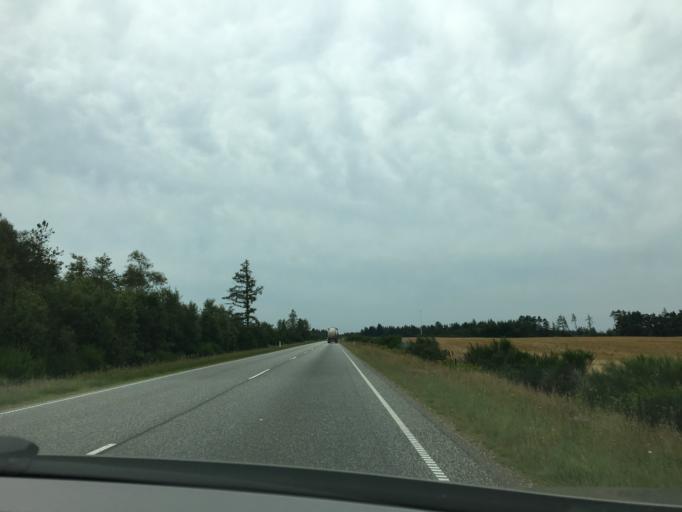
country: DK
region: Central Jutland
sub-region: Herning Kommune
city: Sunds
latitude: 56.3468
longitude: 8.9762
